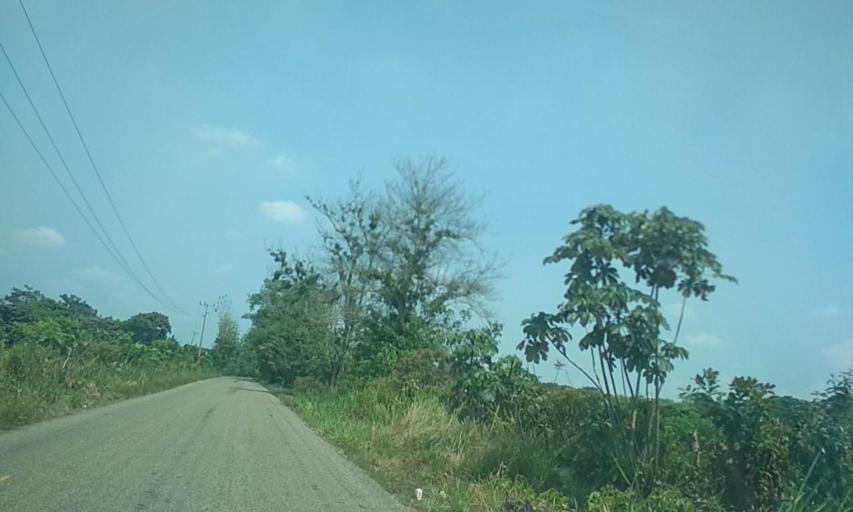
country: MX
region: Tabasco
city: Huimanguillo
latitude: 17.8191
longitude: -93.5010
